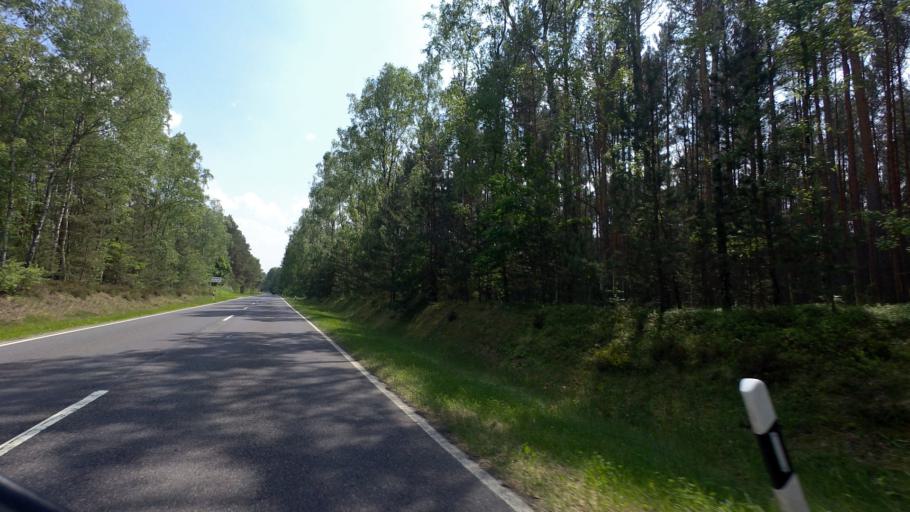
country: DE
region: Saxony
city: Schleife
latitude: 51.5549
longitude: 14.5016
